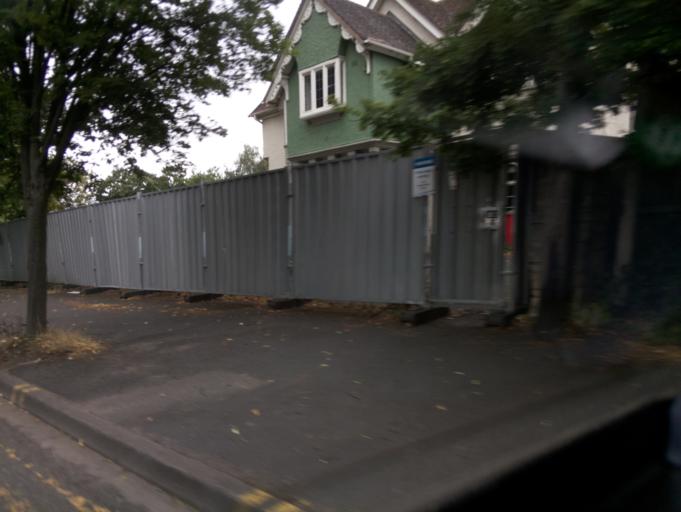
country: GB
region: England
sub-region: Worcestershire
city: Worcester
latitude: 52.2162
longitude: -2.2201
